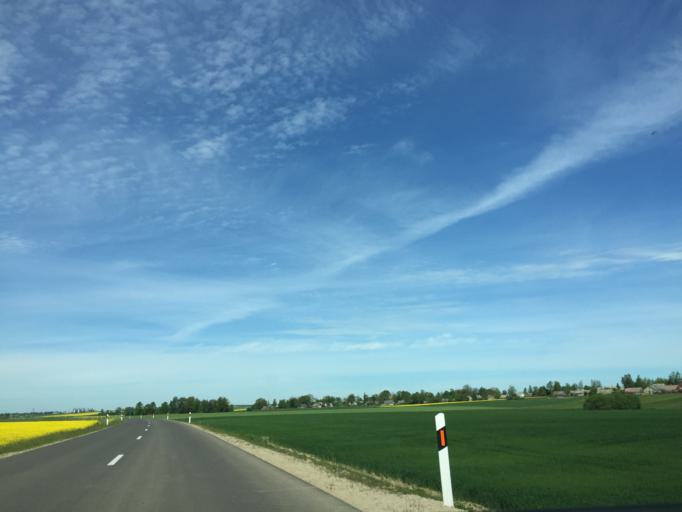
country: LT
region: Panevezys
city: Pasvalys
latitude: 56.1139
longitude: 24.2266
